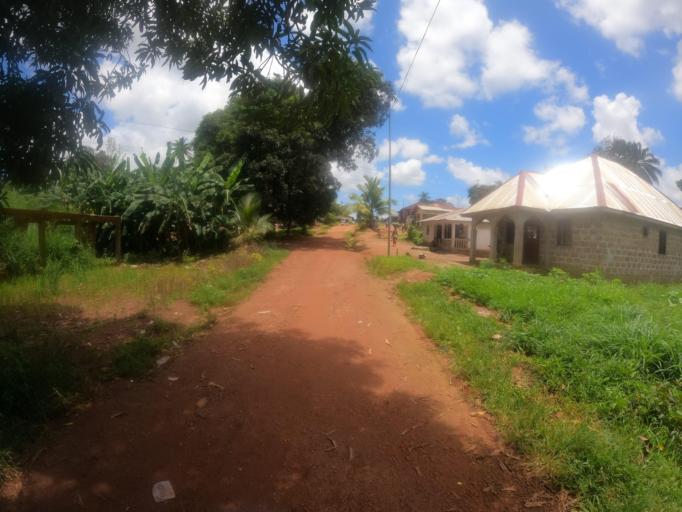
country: SL
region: Northern Province
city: Makeni
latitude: 8.8867
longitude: -12.0726
